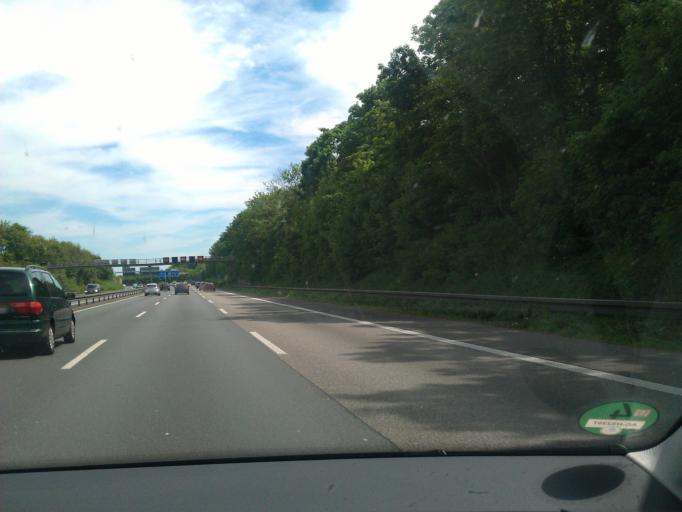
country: DE
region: North Rhine-Westphalia
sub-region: Regierungsbezirk Dusseldorf
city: Neuss
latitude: 51.1770
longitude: 6.6893
